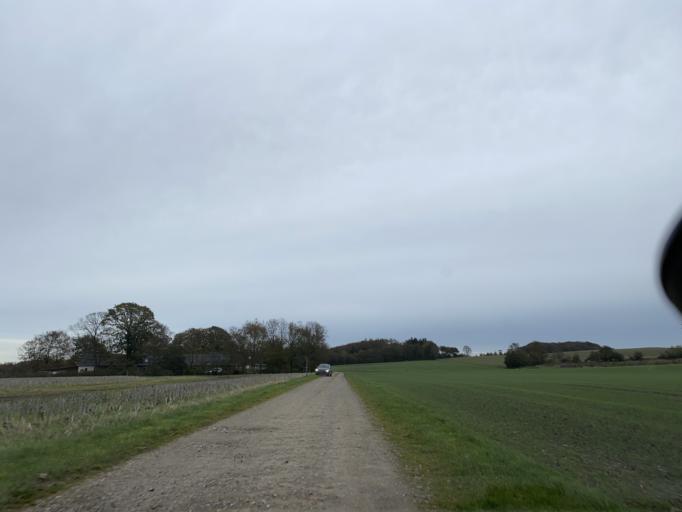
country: DK
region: Central Jutland
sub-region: Skanderborg Kommune
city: Ry
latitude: 56.1908
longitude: 9.7805
